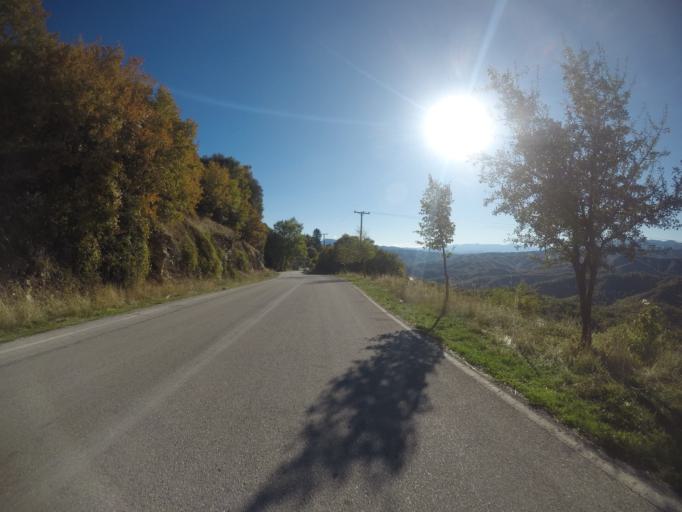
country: GR
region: Epirus
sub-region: Nomos Ioanninon
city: Asprangeloi
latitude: 39.8739
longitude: 20.7466
